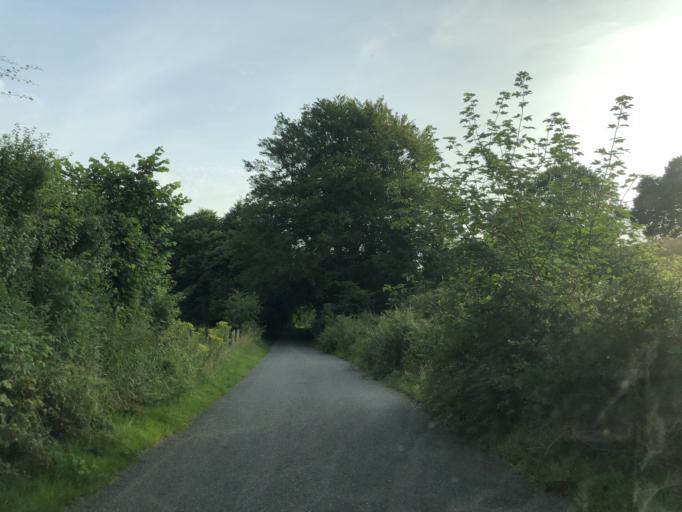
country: DK
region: South Denmark
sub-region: Fredericia Kommune
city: Taulov
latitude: 55.5875
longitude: 9.6208
